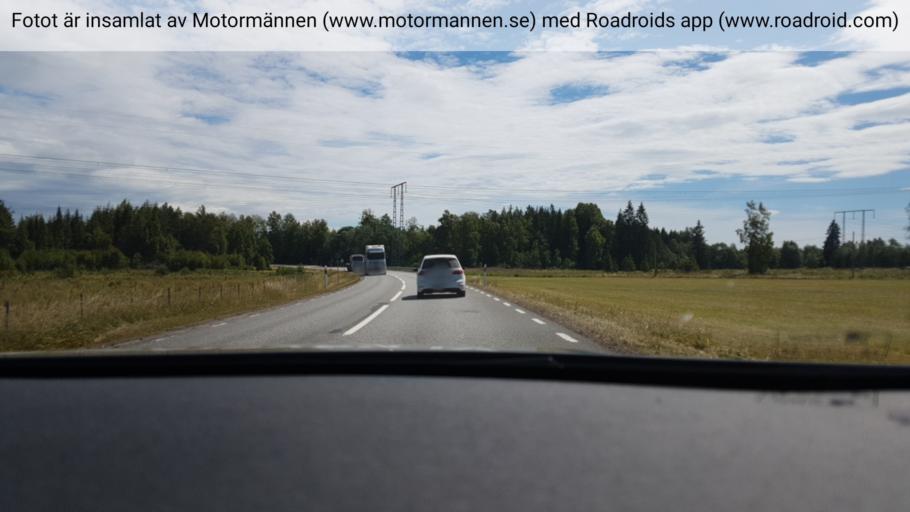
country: SE
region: Joenkoeping
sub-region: Aneby Kommun
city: Aneby
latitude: 57.9761
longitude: 14.7709
